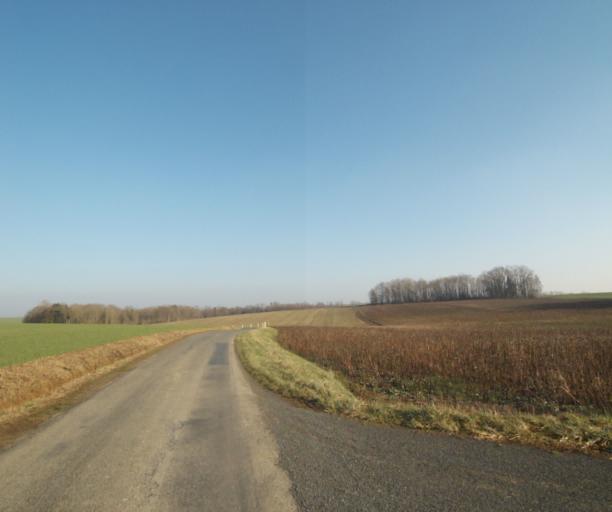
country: FR
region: Champagne-Ardenne
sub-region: Departement de la Haute-Marne
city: Bienville
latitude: 48.5483
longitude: 5.0374
